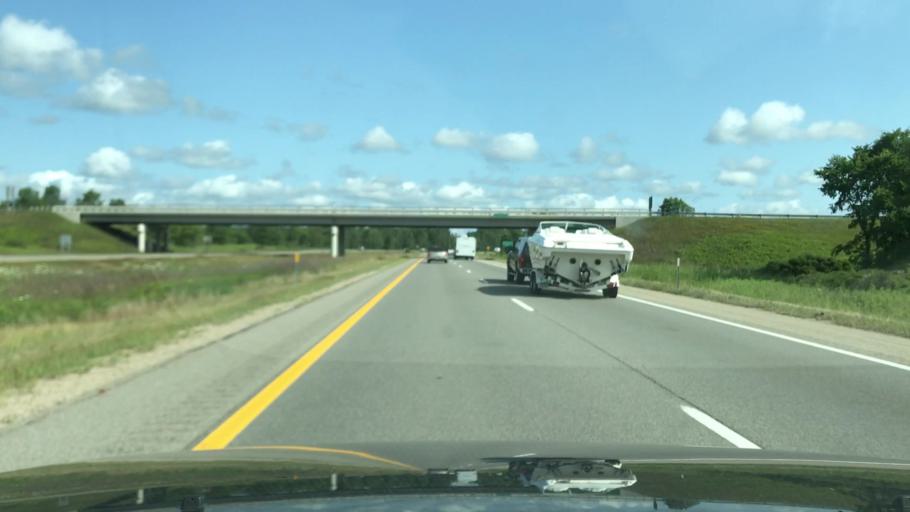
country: US
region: Michigan
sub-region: Kent County
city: Cedar Springs
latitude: 43.2928
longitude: -85.5421
